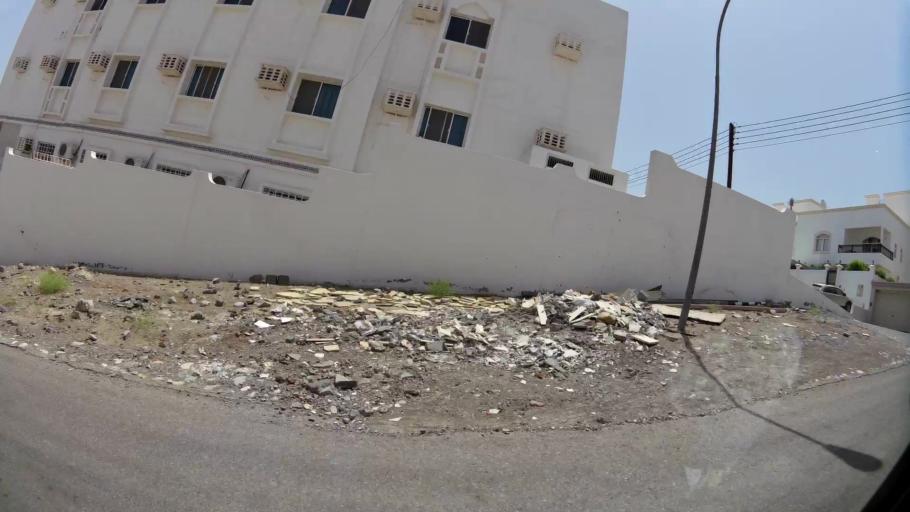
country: OM
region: Muhafazat Masqat
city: Bawshar
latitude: 23.5816
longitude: 58.4362
